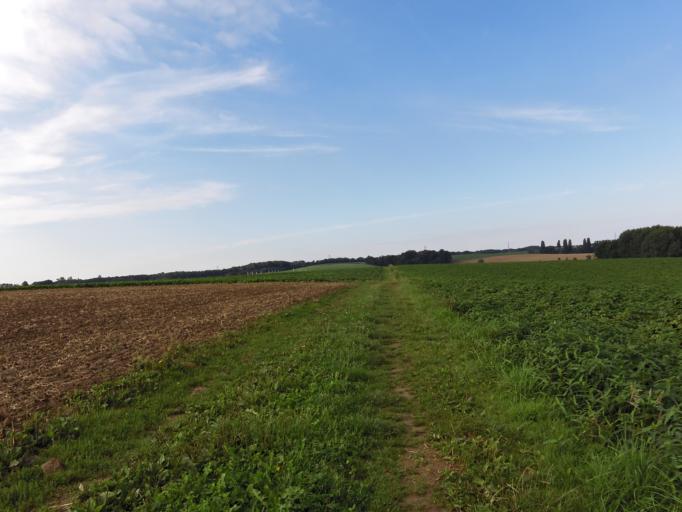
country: NL
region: Limburg
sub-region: Gemeente Voerendaal
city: Klimmen
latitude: 50.8916
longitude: 5.8908
